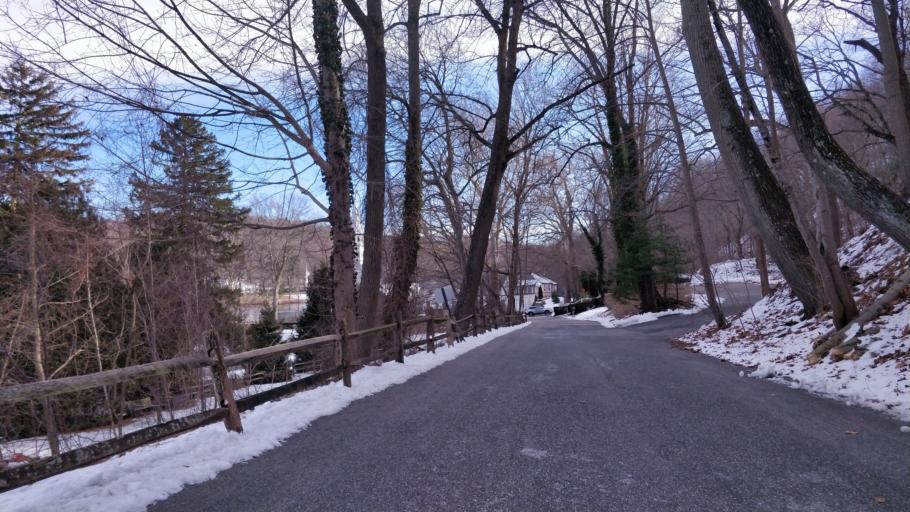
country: US
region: New York
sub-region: Nassau County
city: Laurel Hollow
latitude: 40.8572
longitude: -73.4653
